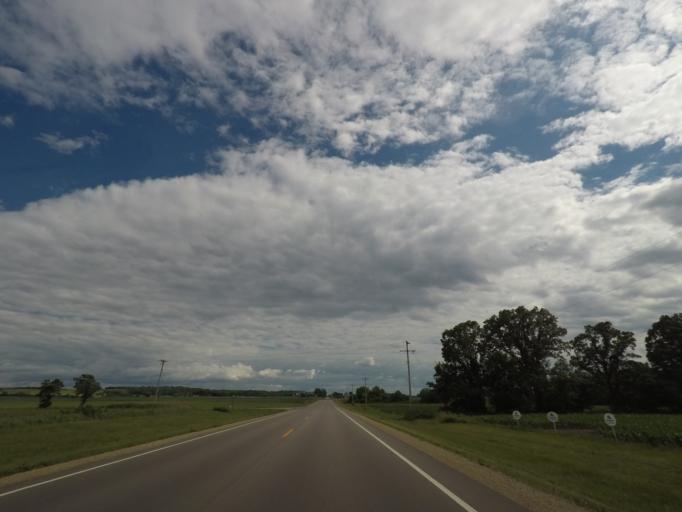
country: US
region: Wisconsin
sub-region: Green County
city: Albany
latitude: 42.7240
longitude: -89.3684
